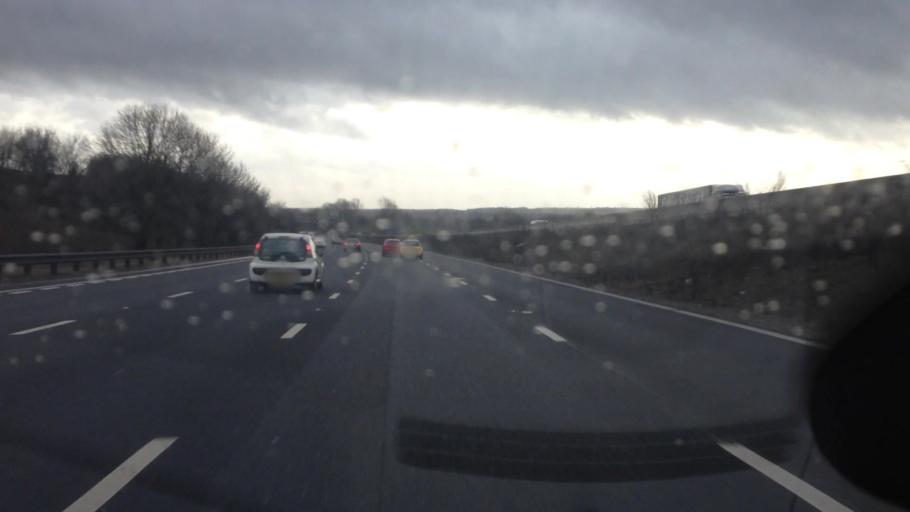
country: GB
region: England
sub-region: City and Borough of Wakefield
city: Horbury
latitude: 53.6749
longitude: -1.5516
